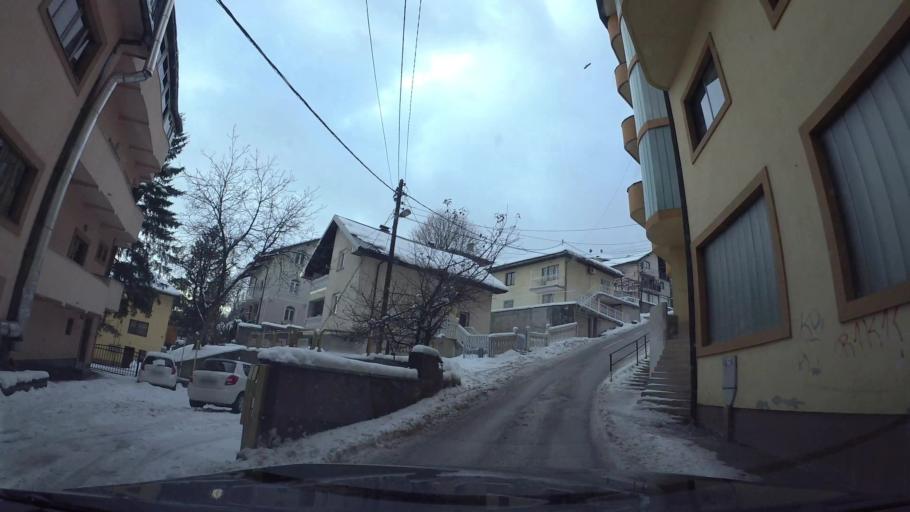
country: BA
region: Federation of Bosnia and Herzegovina
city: Kobilja Glava
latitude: 43.8598
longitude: 18.3871
